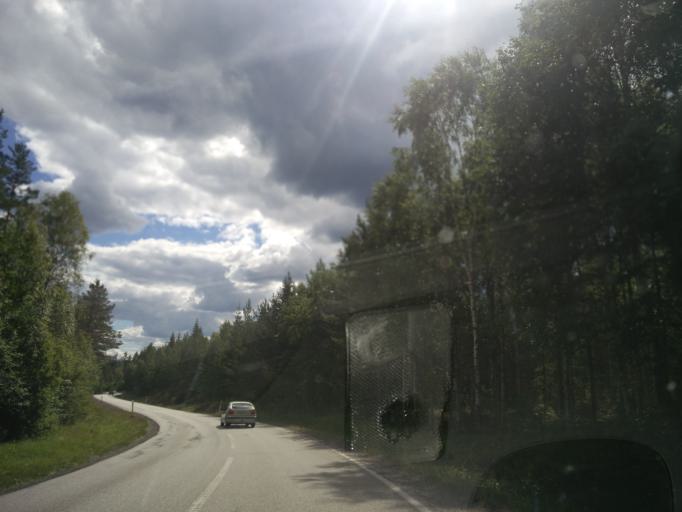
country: SE
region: OErebro
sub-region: Ljusnarsbergs Kommun
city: Kopparberg
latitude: 59.8410
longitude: 14.9970
